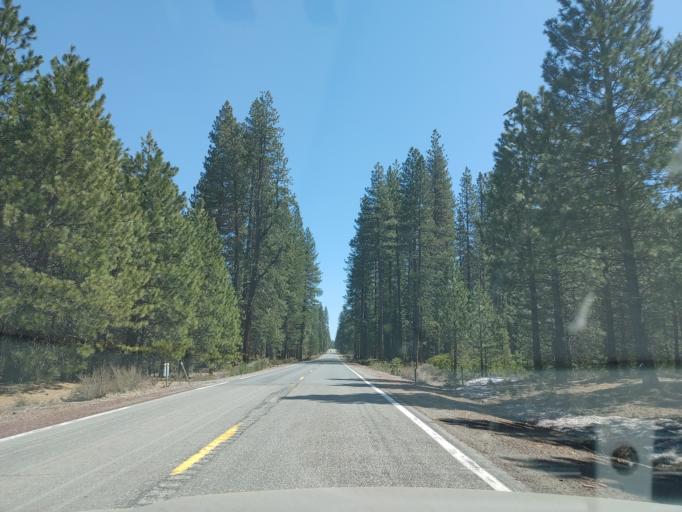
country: US
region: California
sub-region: Siskiyou County
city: McCloud
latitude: 41.2648
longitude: -121.9346
